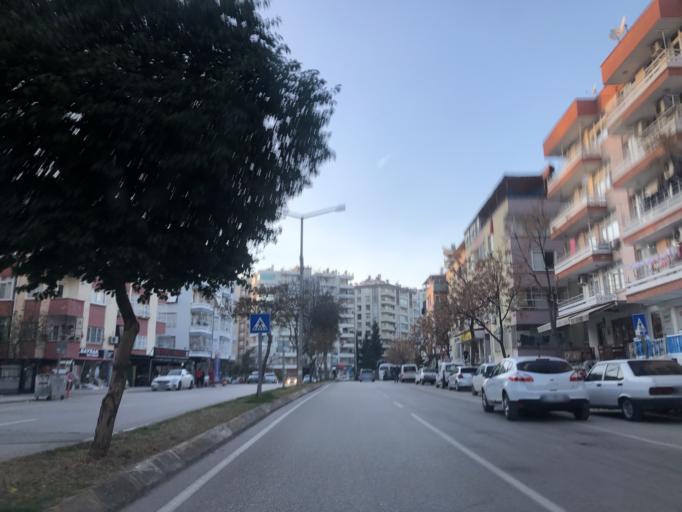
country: TR
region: Adana
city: Adana
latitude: 37.0428
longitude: 35.3001
